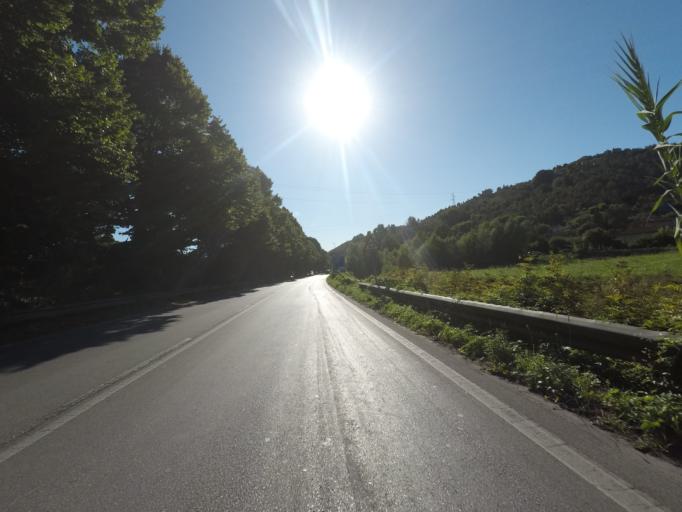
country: IT
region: Tuscany
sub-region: Provincia di Lucca
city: Piano di Mommio
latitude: 43.9363
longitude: 10.2872
